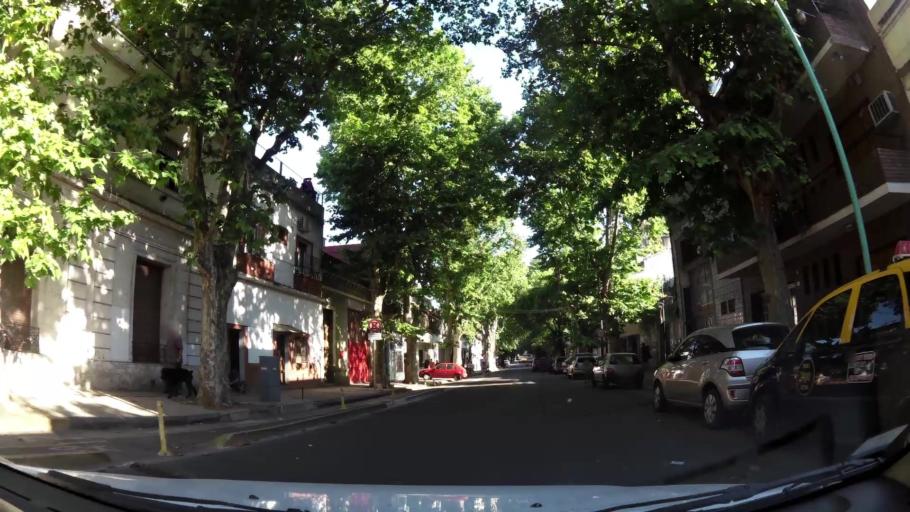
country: AR
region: Buenos Aires F.D.
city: Buenos Aires
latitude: -34.6251
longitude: -58.4231
